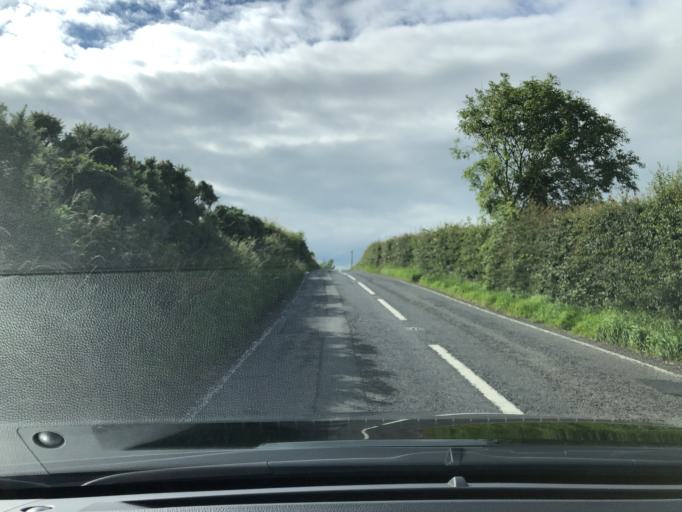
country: GB
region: Northern Ireland
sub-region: Down District
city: Dundrum
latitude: 54.2762
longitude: -5.7970
